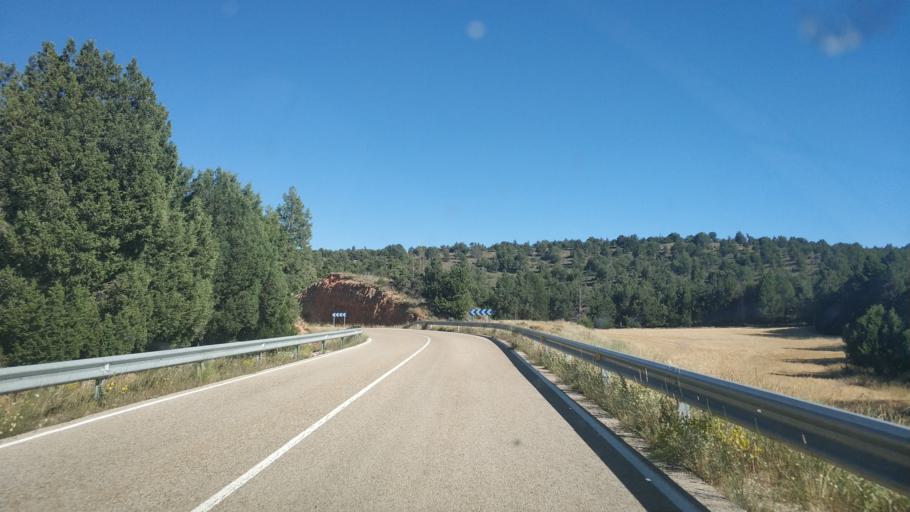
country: ES
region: Castille and Leon
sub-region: Provincia de Soria
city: Liceras
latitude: 41.4345
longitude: -3.2100
